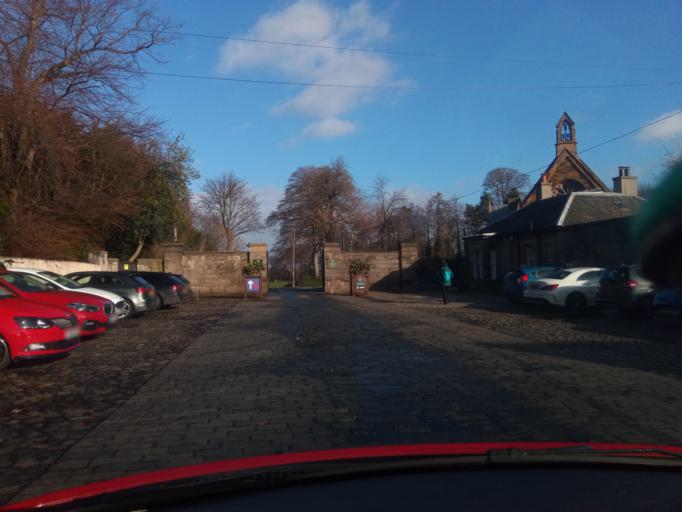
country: GB
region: Scotland
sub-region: Midlothian
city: Dalkeith
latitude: 55.8976
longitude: -3.0665
